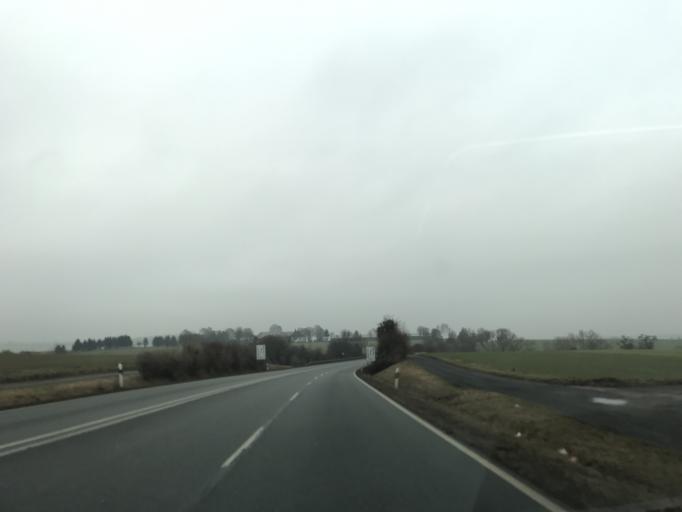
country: DE
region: Hesse
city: Grebenstein
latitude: 51.4617
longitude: 9.4057
